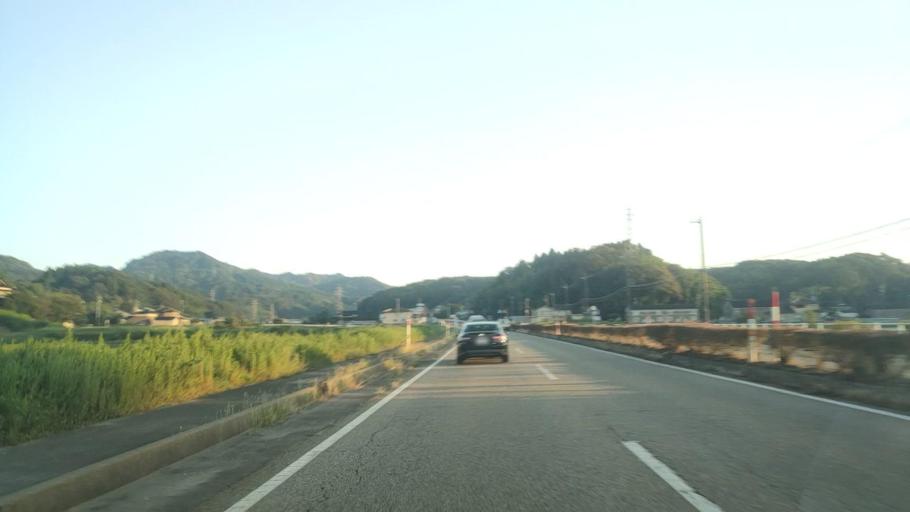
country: JP
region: Toyama
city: Himi
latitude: 36.8125
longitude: 136.9964
